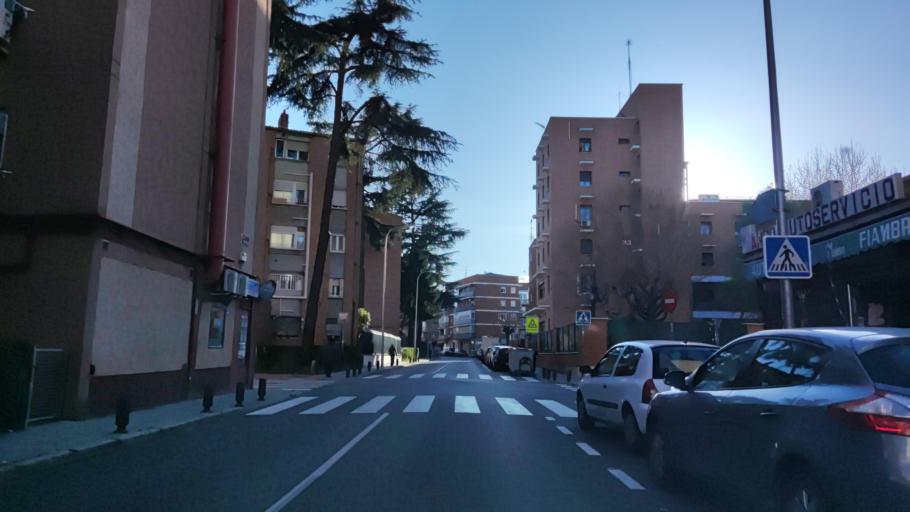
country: ES
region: Madrid
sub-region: Provincia de Madrid
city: Latina
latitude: 40.3978
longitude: -3.7690
